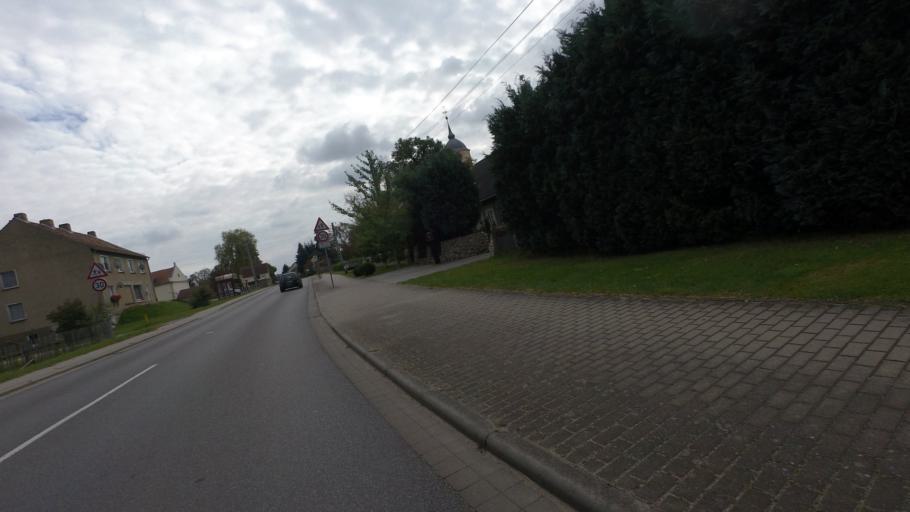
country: DE
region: Brandenburg
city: Golssen
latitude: 51.9512
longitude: 13.6433
